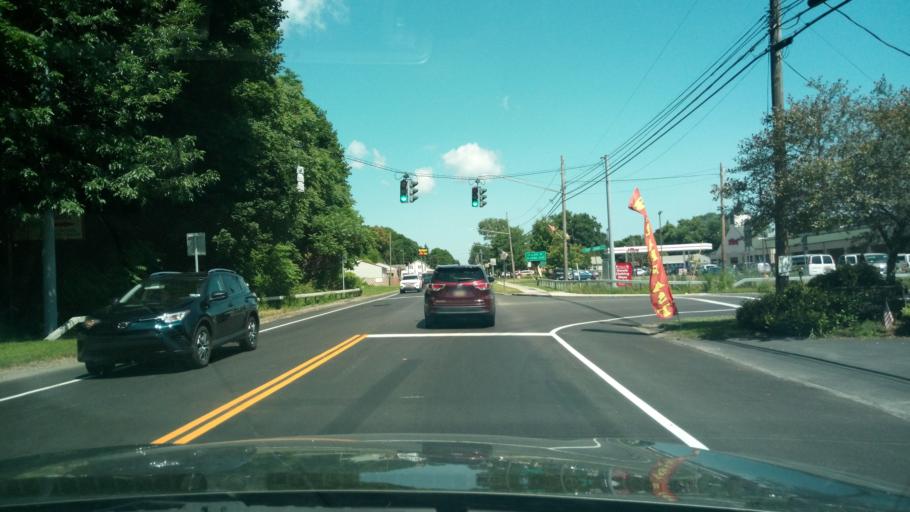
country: US
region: New York
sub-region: Schuyler County
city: Watkins Glen
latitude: 42.3684
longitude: -76.8669
